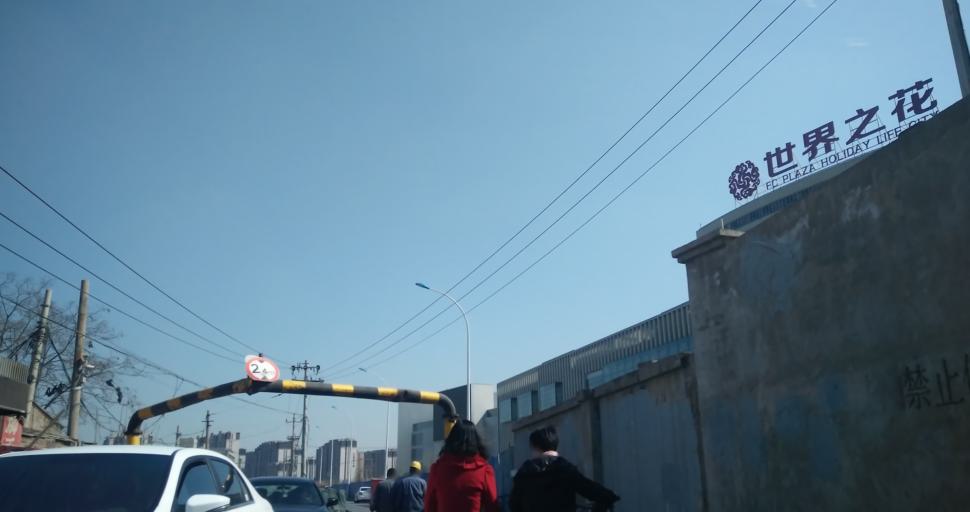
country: CN
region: Beijing
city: Dahongmen
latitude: 39.8190
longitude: 116.4127
